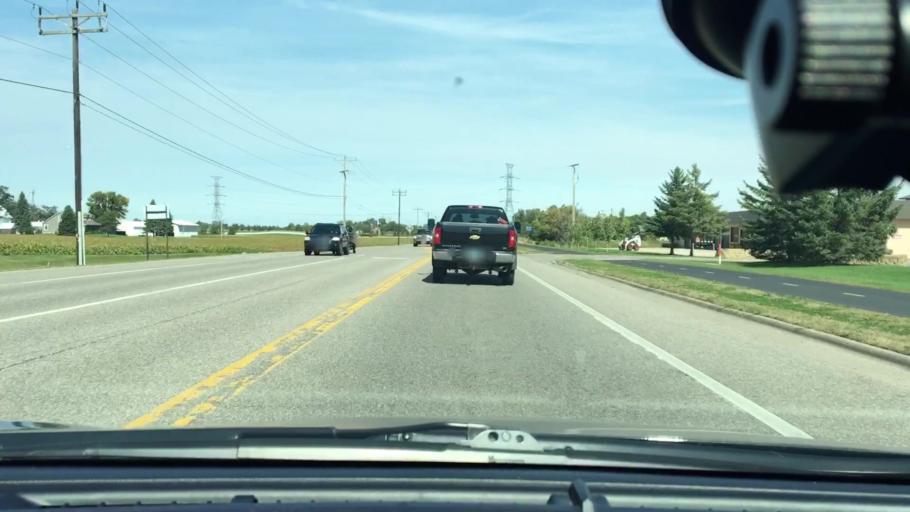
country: US
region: Minnesota
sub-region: Wright County
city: Hanover
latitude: 45.1241
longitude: -93.6358
